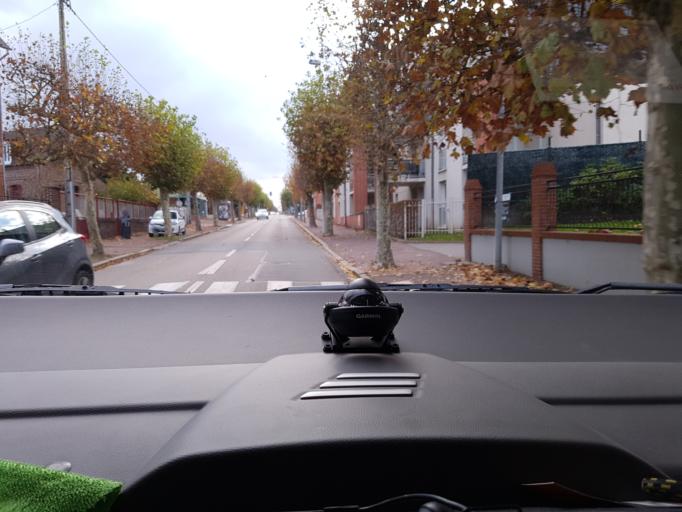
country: FR
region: Haute-Normandie
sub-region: Departement de la Seine-Maritime
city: Rouxmesnil-Bouteilles
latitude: 49.9144
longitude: 1.0736
